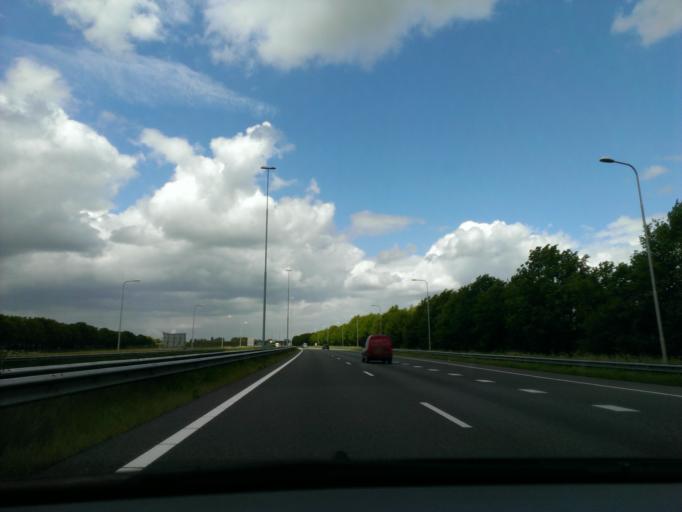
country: NL
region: North Brabant
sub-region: Gemeente Cuijk
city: Cuijk
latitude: 51.6960
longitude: 5.8854
